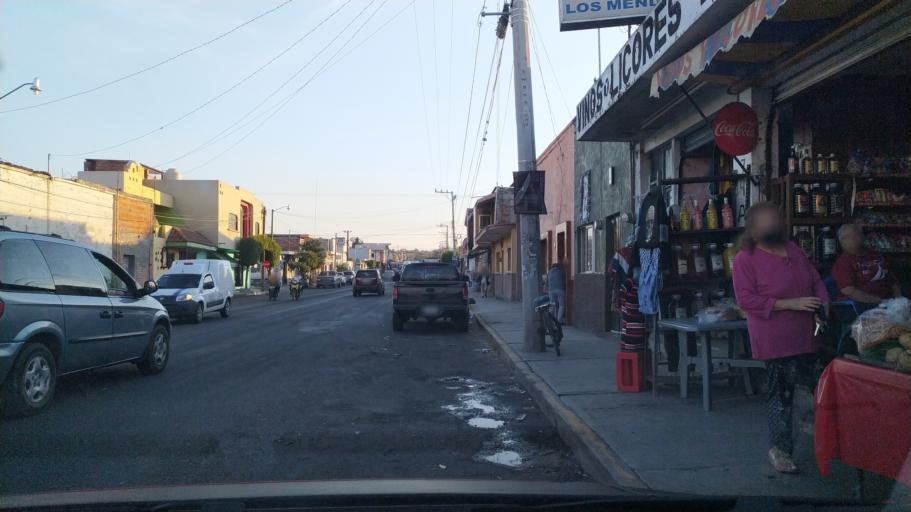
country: MX
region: Michoacan
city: Vistahermosa de Negrete
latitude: 20.2696
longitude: -102.4742
